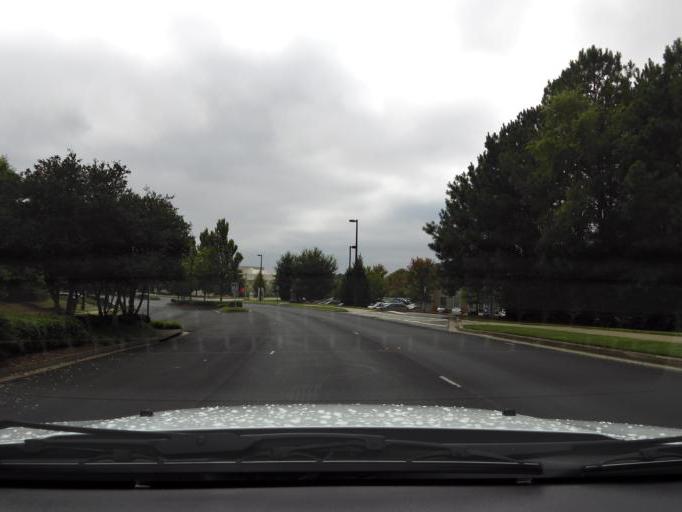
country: US
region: Georgia
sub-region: Cobb County
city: Kennesaw
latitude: 34.0396
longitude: -84.5743
